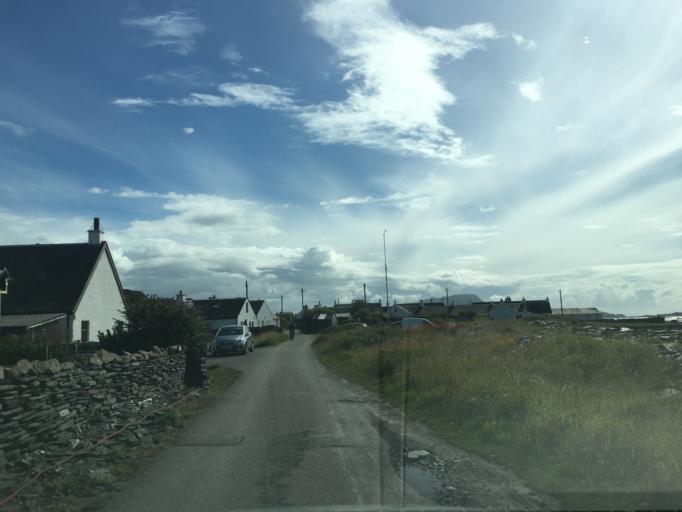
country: GB
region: Scotland
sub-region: Argyll and Bute
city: Isle Of Mull
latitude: 56.2572
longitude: -5.6518
